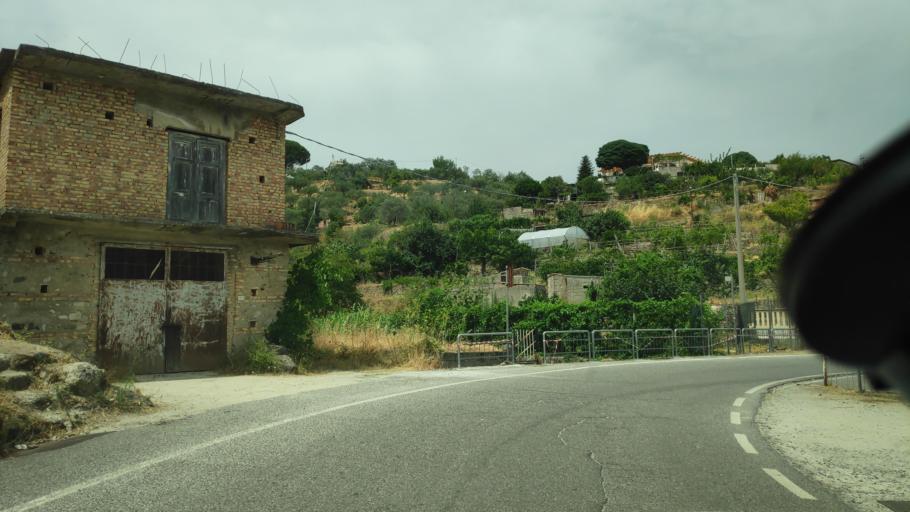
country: IT
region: Calabria
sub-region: Provincia di Catanzaro
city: Davoli
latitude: 38.6511
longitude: 16.4848
